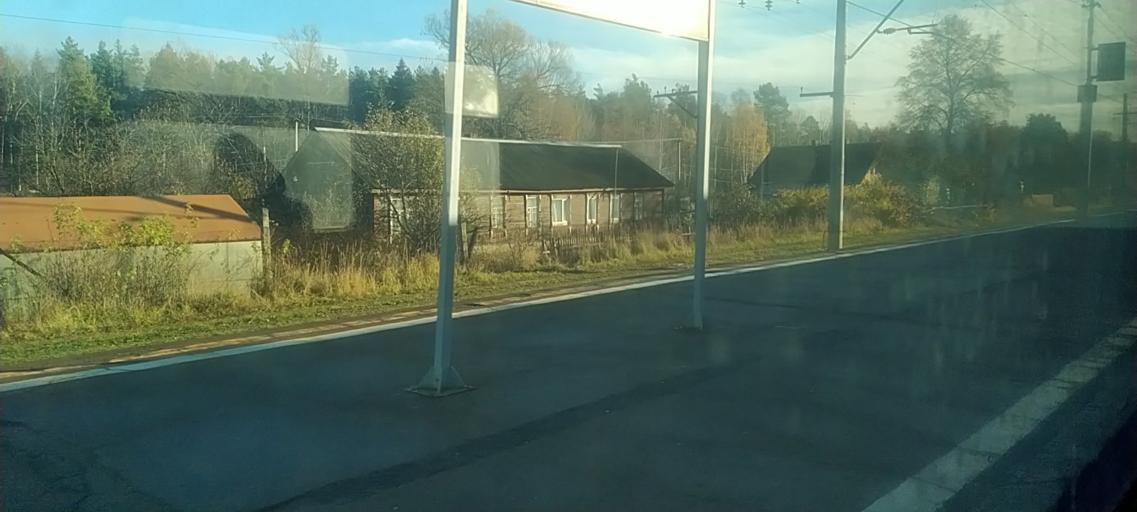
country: RU
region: Moskovskaya
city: Ramenskoye
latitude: 55.6363
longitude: 38.2739
